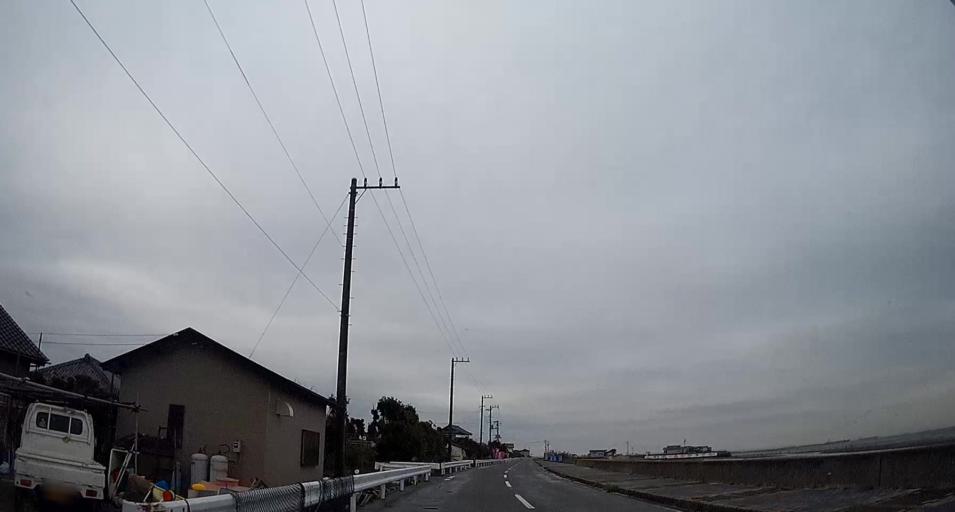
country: JP
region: Chiba
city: Kisarazu
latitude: 35.4332
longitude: 139.9094
